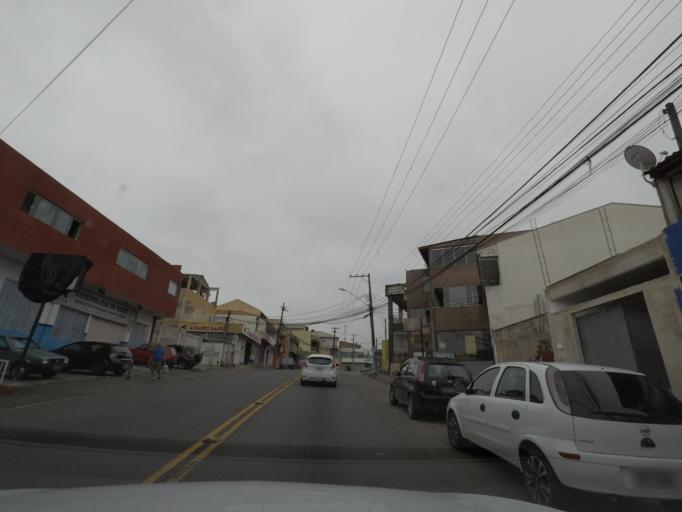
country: BR
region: Parana
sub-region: Curitiba
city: Curitiba
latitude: -25.4610
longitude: -49.3428
